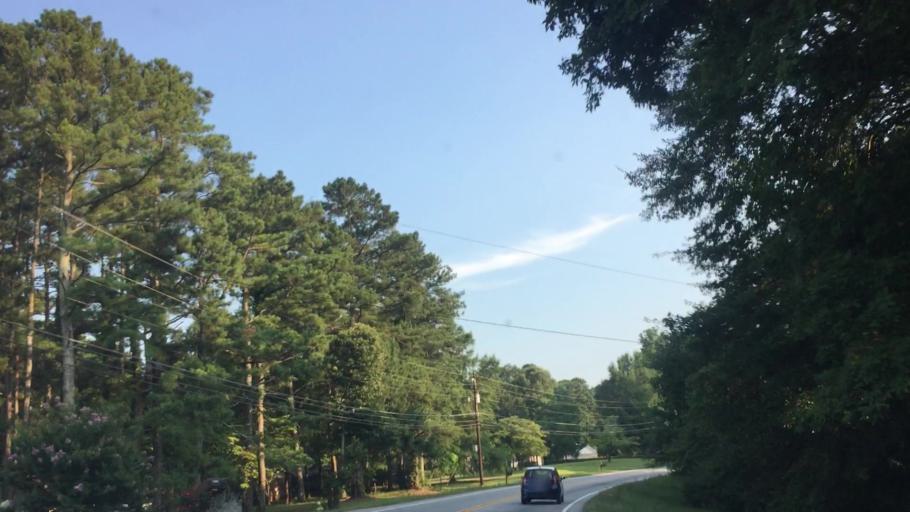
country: US
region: Georgia
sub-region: DeKalb County
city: Pine Mountain
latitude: 33.6728
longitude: -84.1956
